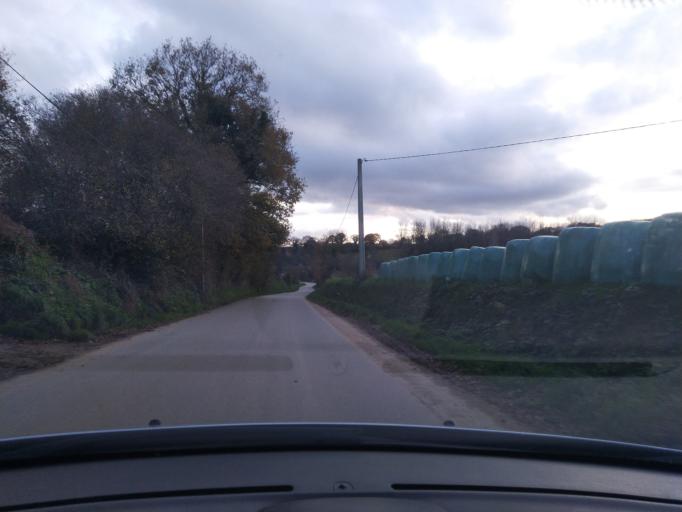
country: FR
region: Brittany
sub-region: Departement du Finistere
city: Guerlesquin
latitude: 48.5581
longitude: -3.6179
